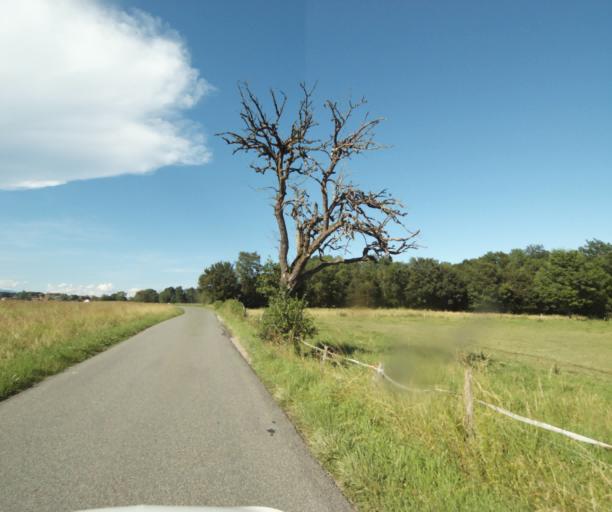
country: FR
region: Rhone-Alpes
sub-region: Departement de la Haute-Savoie
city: Massongy
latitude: 46.3391
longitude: 6.3275
